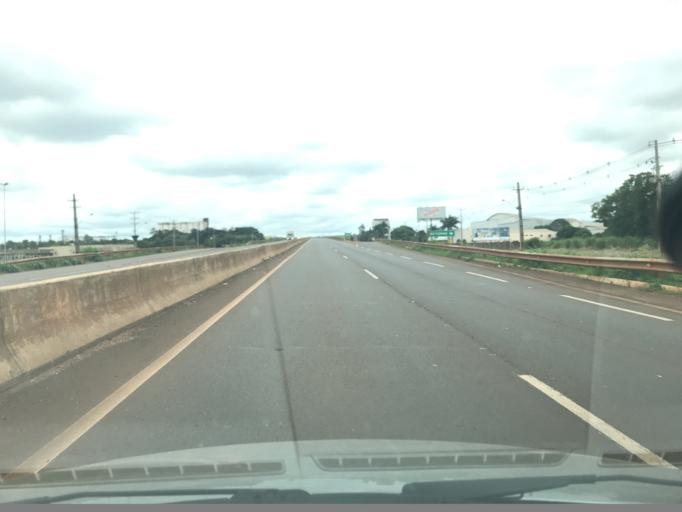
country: BR
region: Parana
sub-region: Paicandu
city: Paicandu
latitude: -23.4526
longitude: -52.0094
